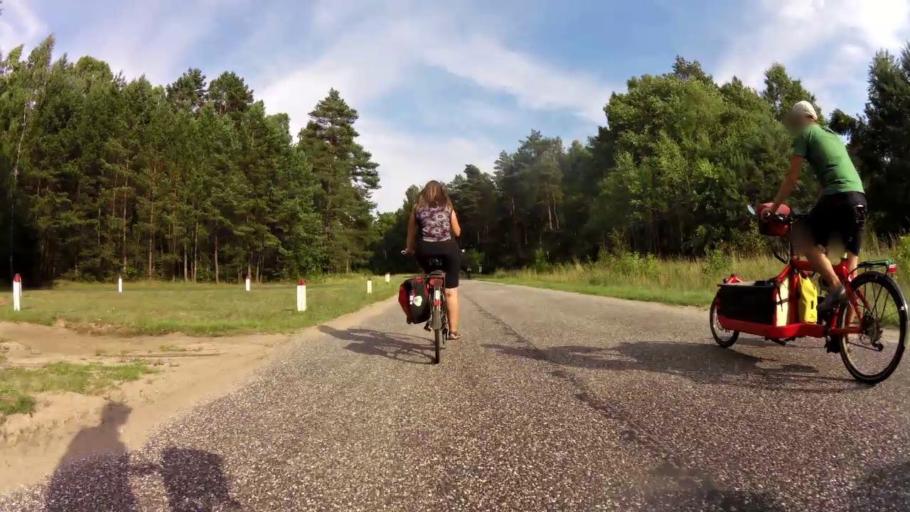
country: PL
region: West Pomeranian Voivodeship
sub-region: Powiat drawski
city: Drawsko Pomorskie
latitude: 53.4699
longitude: 15.7298
